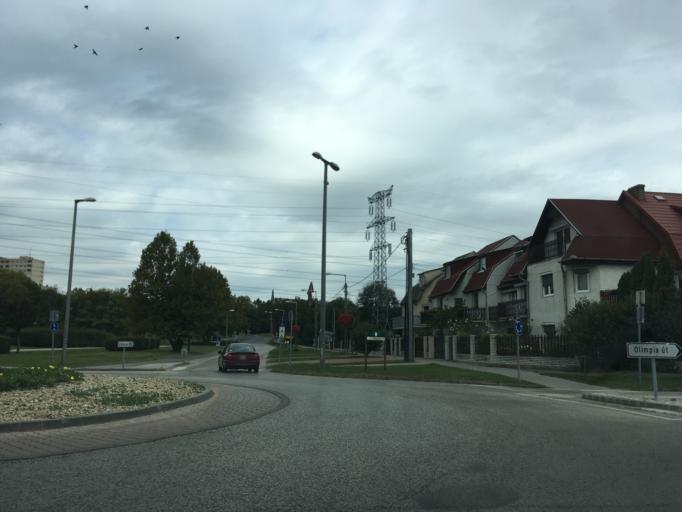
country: HU
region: Pest
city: Szazhalombatta
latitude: 47.3151
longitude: 18.9147
